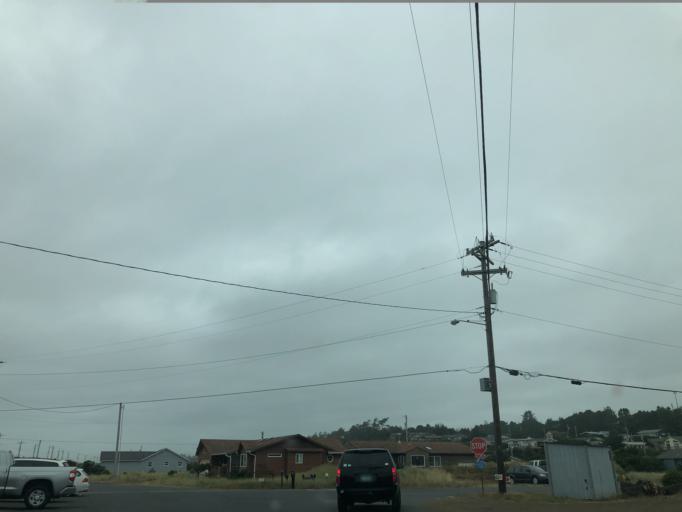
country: US
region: Oregon
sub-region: Lincoln County
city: Waldport
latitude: 44.4365
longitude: -124.0820
